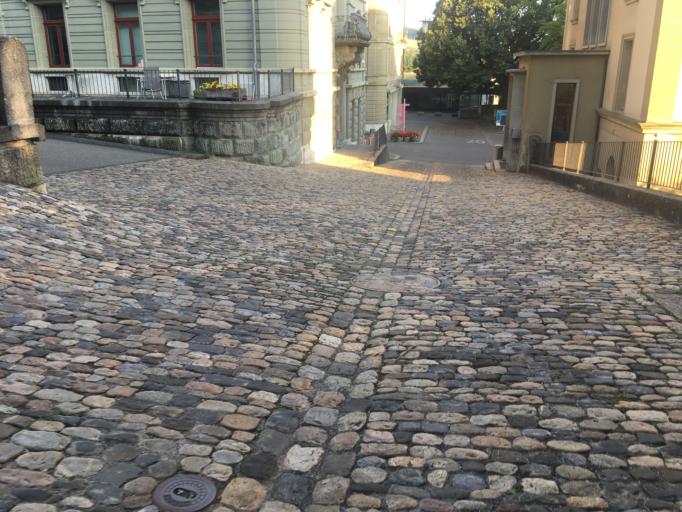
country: CH
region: Bern
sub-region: Emmental District
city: Burgdorf
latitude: 47.0557
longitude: 7.6249
